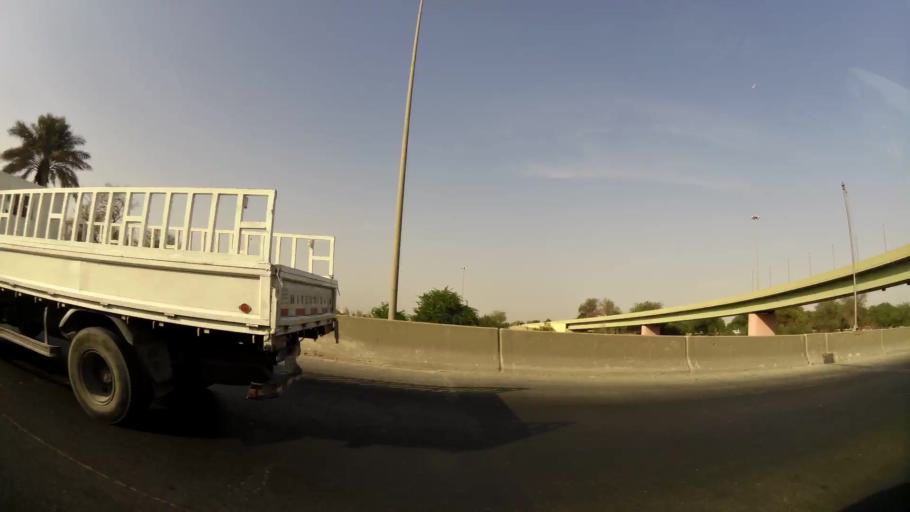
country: KW
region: Al Farwaniyah
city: Janub as Surrah
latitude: 29.2517
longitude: 47.9887
